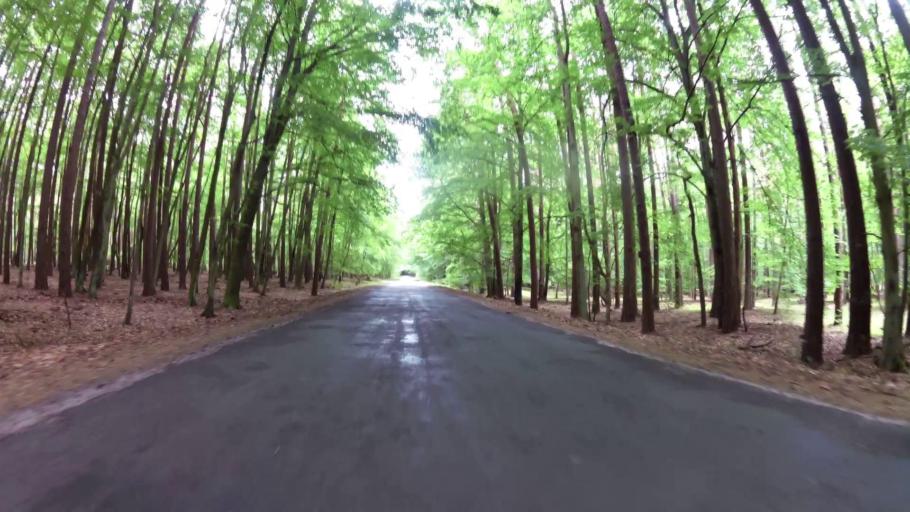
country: PL
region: West Pomeranian Voivodeship
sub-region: Powiat kamienski
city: Miedzyzdroje
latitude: 53.9433
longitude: 14.5509
